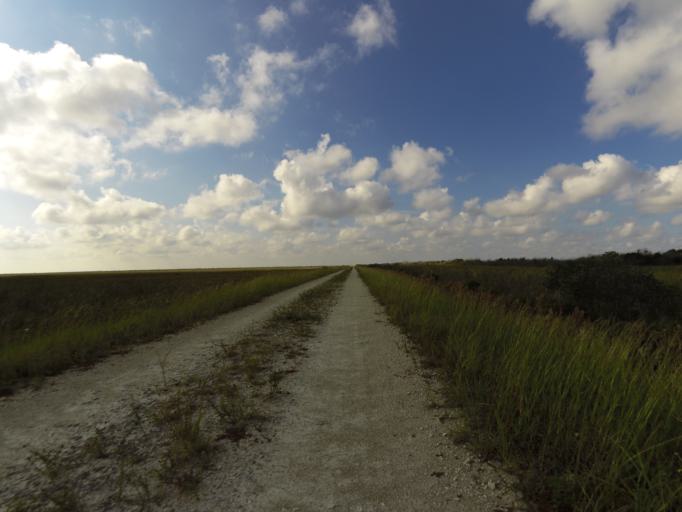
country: US
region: Florida
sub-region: Broward County
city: Weston
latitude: 26.0400
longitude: -80.4883
